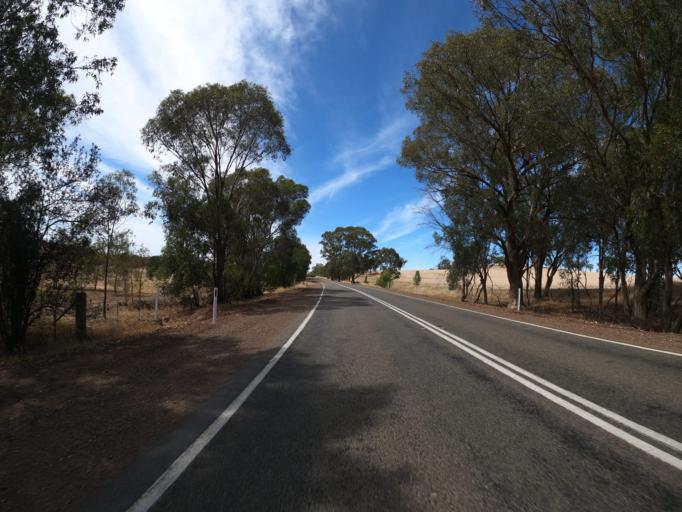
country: AU
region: Victoria
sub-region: Benalla
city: Benalla
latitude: -36.3233
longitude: 145.9588
